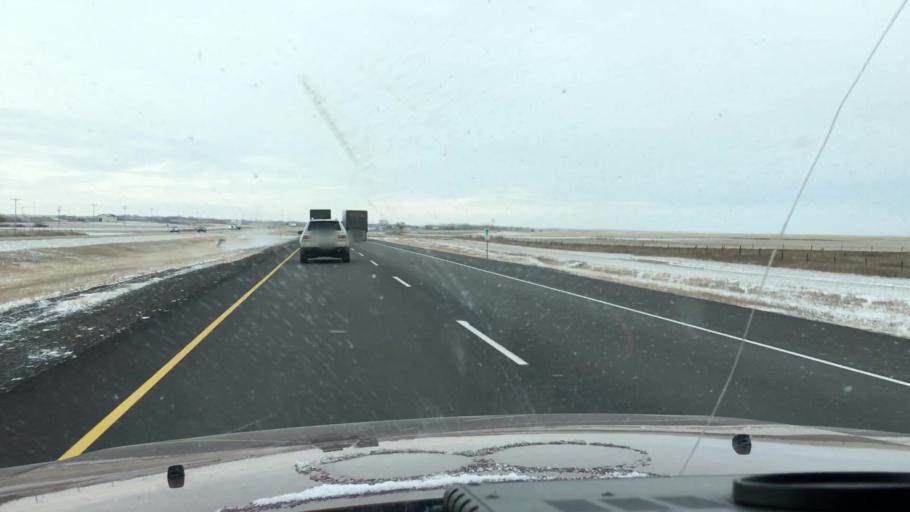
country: CA
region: Saskatchewan
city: Saskatoon
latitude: 51.7843
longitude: -106.4795
